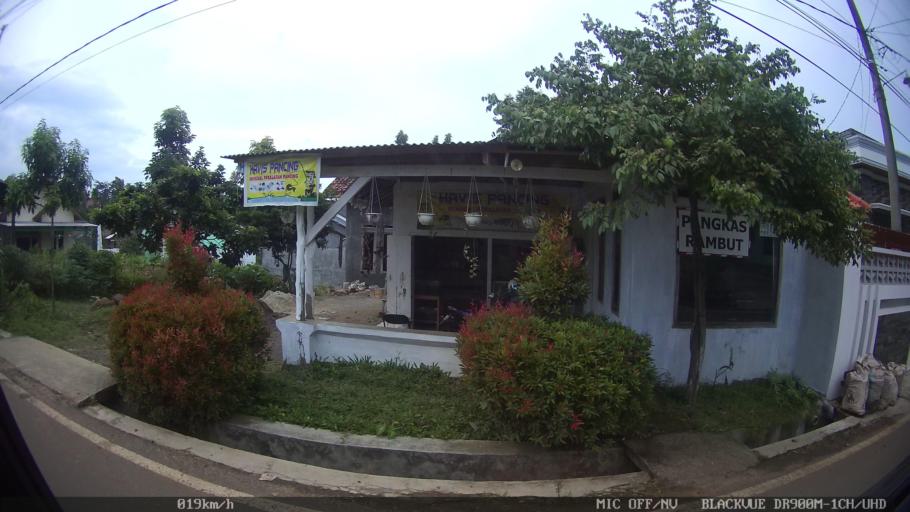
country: ID
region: Lampung
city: Kedaton
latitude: -5.3907
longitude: 105.1951
